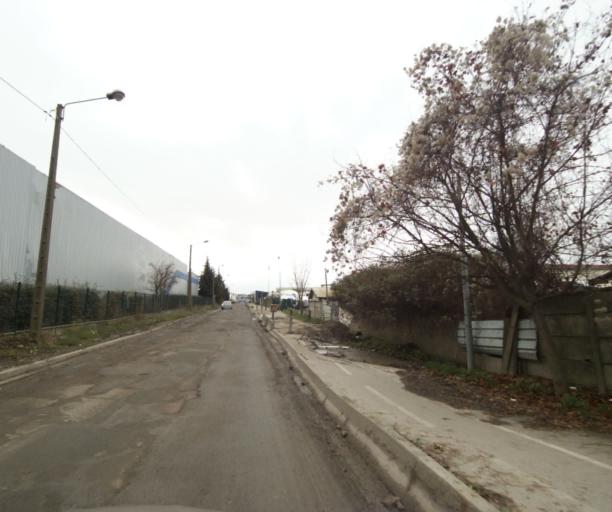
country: FR
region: Ile-de-France
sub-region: Departement du Val-de-Marne
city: Ablon-sur-Seine
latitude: 48.7349
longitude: 2.4301
